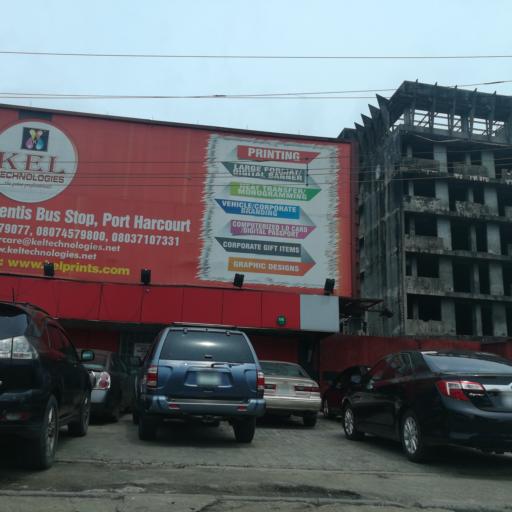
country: NG
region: Rivers
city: Port Harcourt
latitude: 4.7911
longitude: 7.0021
